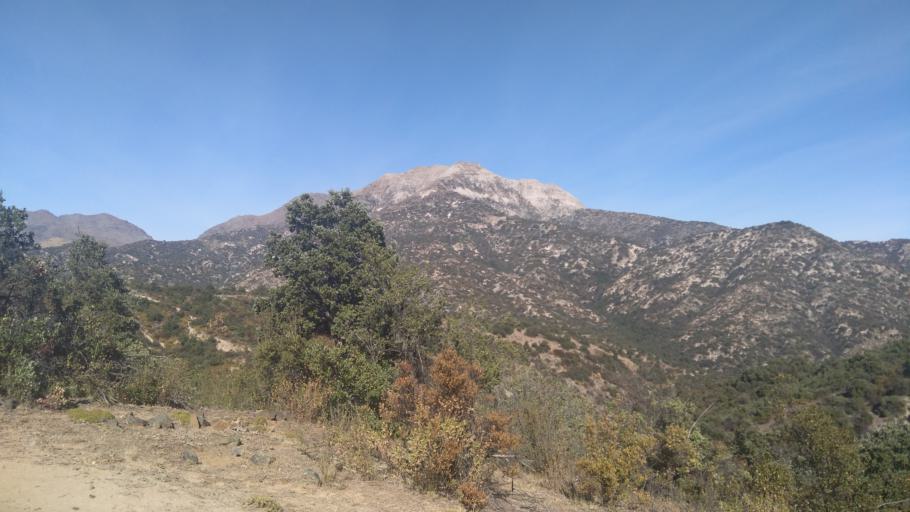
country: CL
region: Santiago Metropolitan
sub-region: Provincia de Cordillera
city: Puente Alto
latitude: -33.7198
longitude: -70.4625
